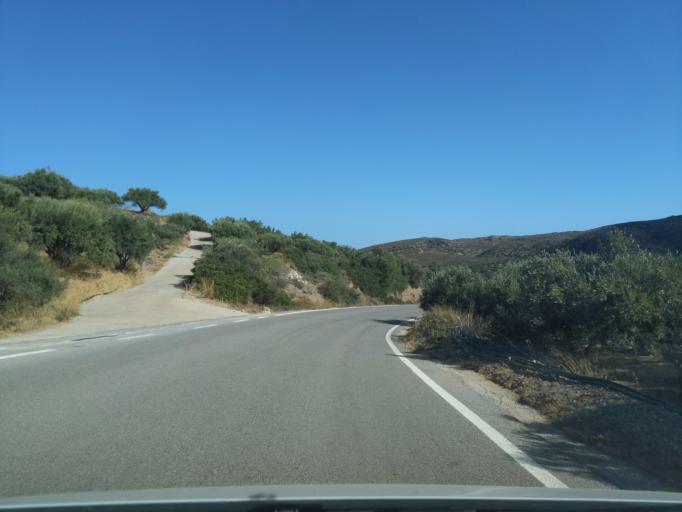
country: GR
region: Crete
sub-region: Nomos Lasithiou
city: Palekastro
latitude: 35.2196
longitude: 26.2583
